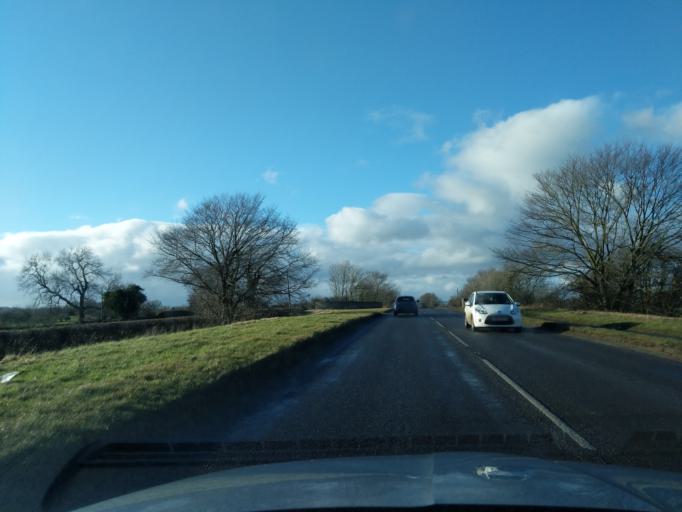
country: GB
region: England
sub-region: North Yorkshire
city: Bedale
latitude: 54.2975
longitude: -1.6163
